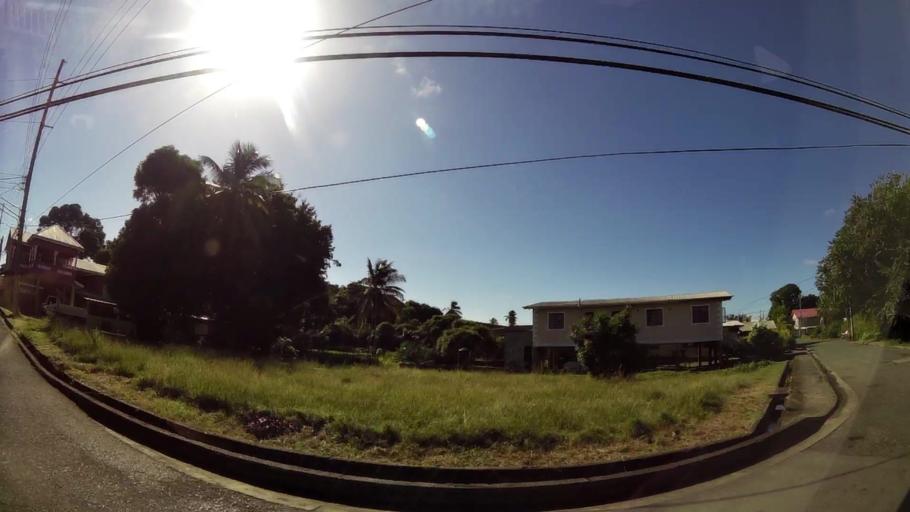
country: TT
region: Tobago
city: Scarborough
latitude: 11.1621
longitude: -60.8101
